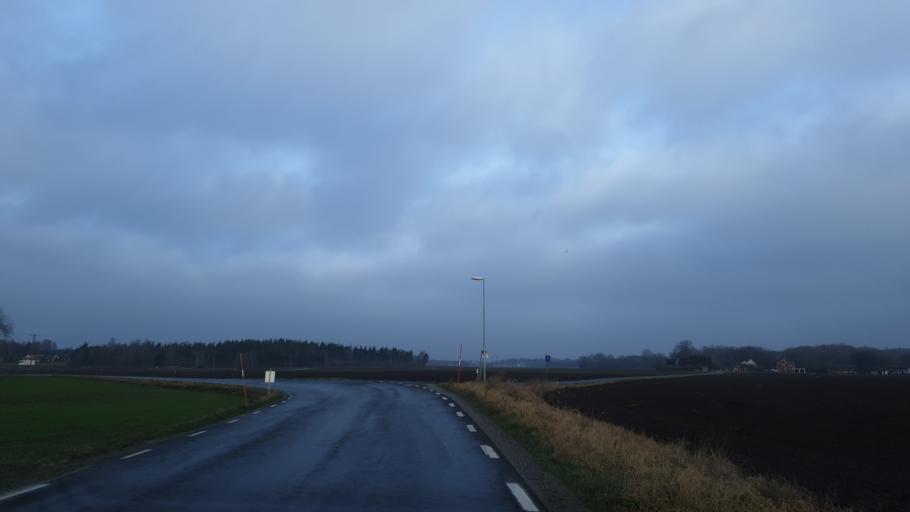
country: SE
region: Blekinge
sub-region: Karlshamns Kommun
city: Morrum
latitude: 56.1670
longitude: 14.7477
